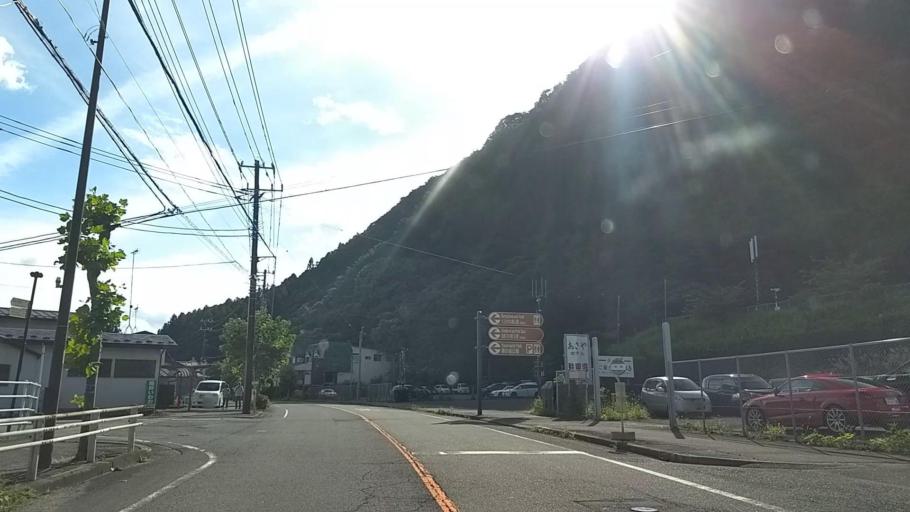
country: JP
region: Tochigi
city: Imaichi
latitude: 36.8352
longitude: 139.7181
